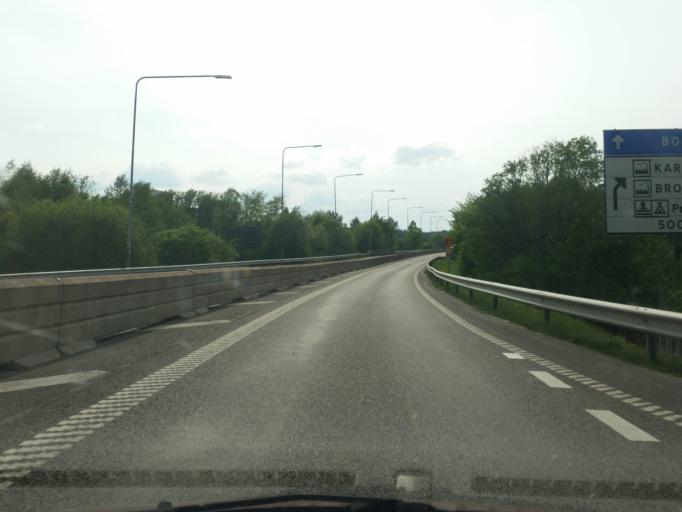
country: SE
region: Vaestra Goetaland
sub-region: Ulricehamns Kommun
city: Ulricehamn
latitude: 57.8033
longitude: 13.4176
